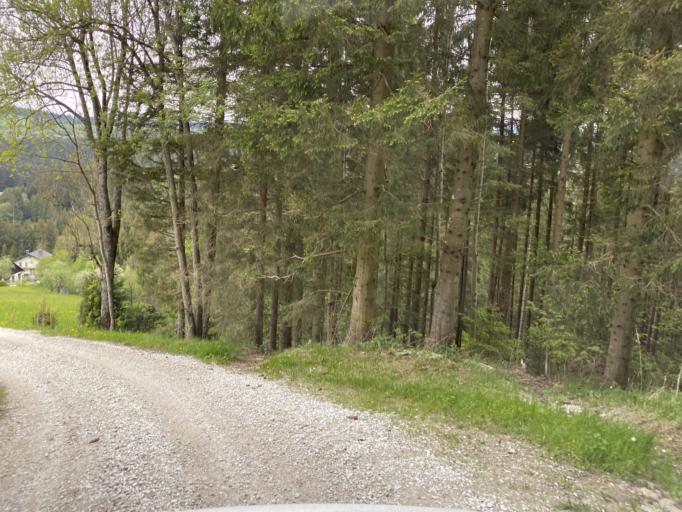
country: AT
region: Styria
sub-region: Politischer Bezirk Weiz
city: Gschaid bei Birkfeld
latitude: 47.3658
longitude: 15.7291
